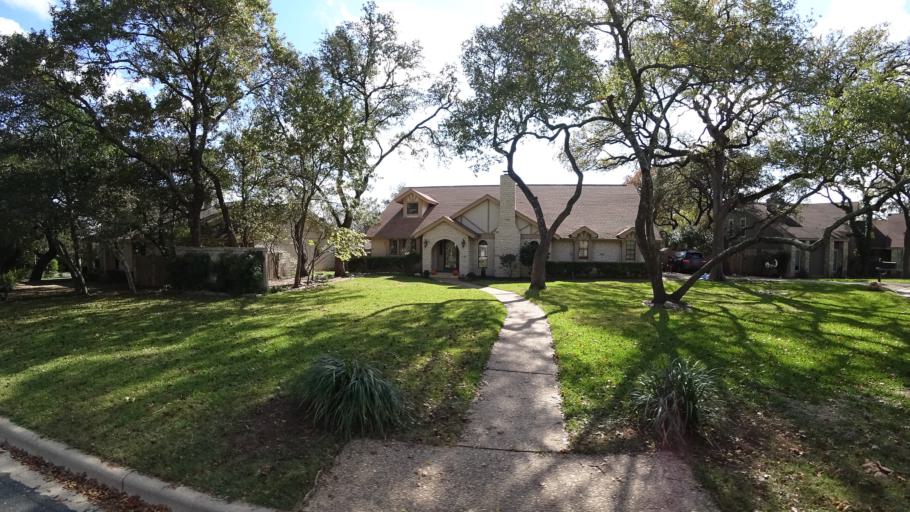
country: US
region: Texas
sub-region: Williamson County
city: Anderson Mill
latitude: 30.4294
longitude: -97.8054
